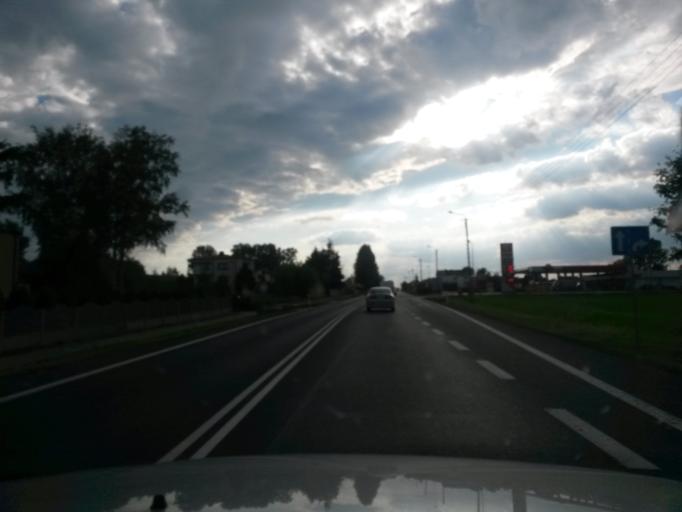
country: PL
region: Lodz Voivodeship
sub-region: Powiat piotrkowski
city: Wola Krzysztoporska
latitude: 51.4153
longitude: 19.5729
